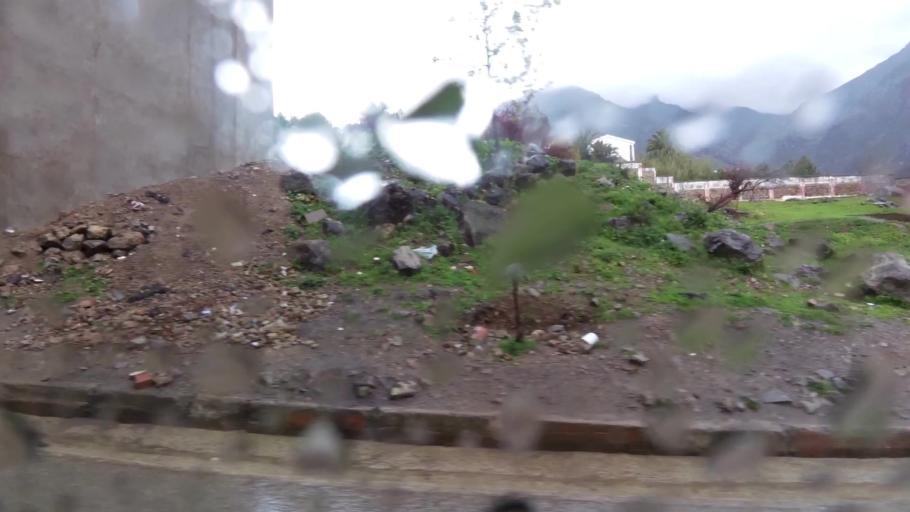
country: MA
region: Tanger-Tetouan
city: Chefchaouene
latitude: 35.1648
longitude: -5.2652
